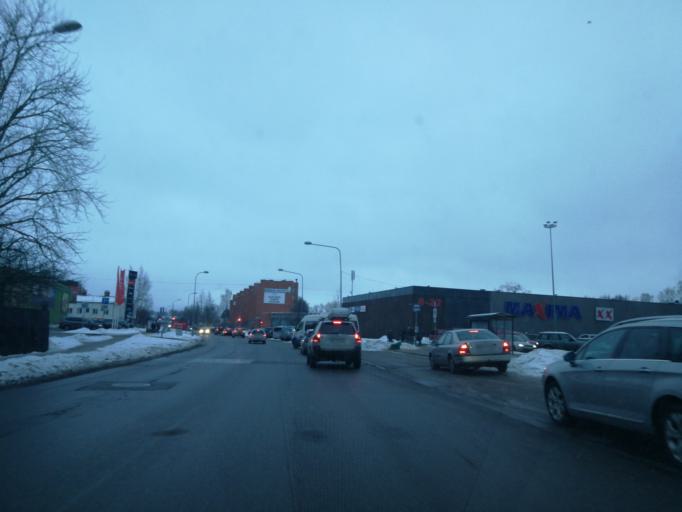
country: LV
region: Riga
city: Riga
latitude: 56.9458
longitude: 24.1718
